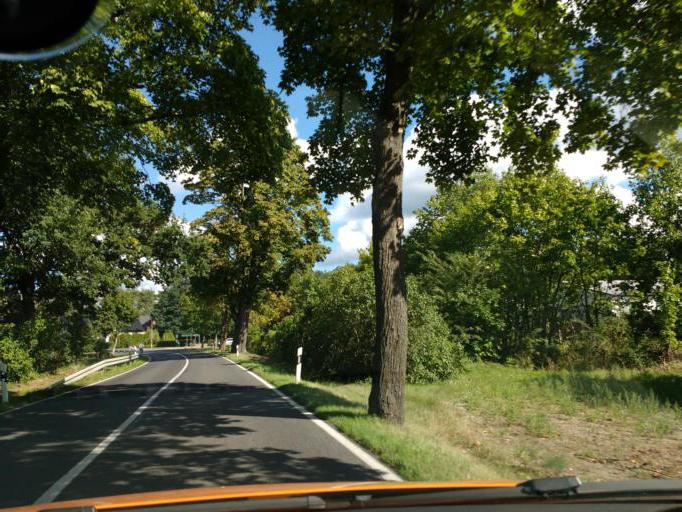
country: DE
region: Brandenburg
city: Bestensee
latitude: 52.2238
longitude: 13.6089
